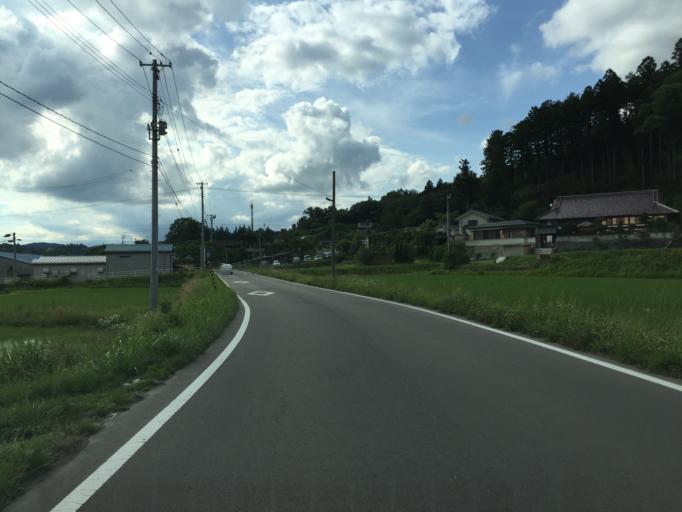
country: JP
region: Fukushima
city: Fukushima-shi
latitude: 37.6758
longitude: 140.5839
